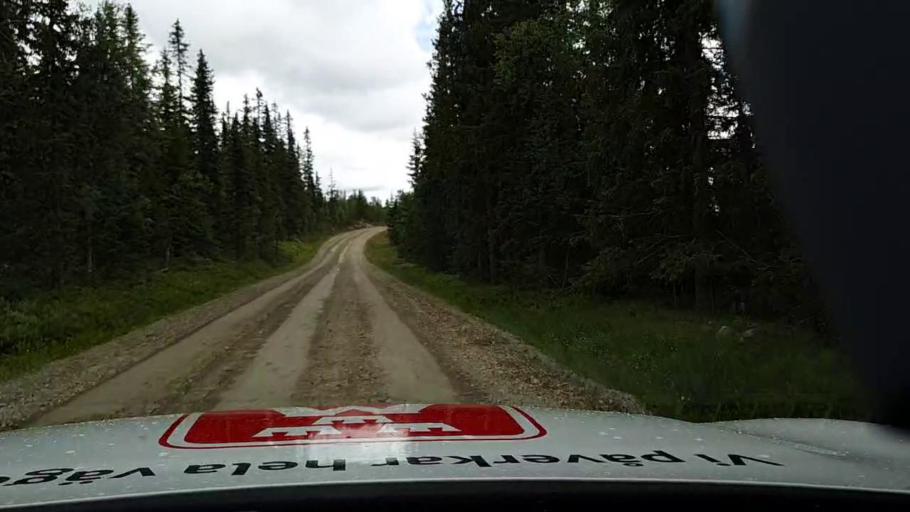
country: SE
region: Jaemtland
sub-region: Are Kommun
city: Jarpen
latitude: 62.6005
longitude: 13.2337
